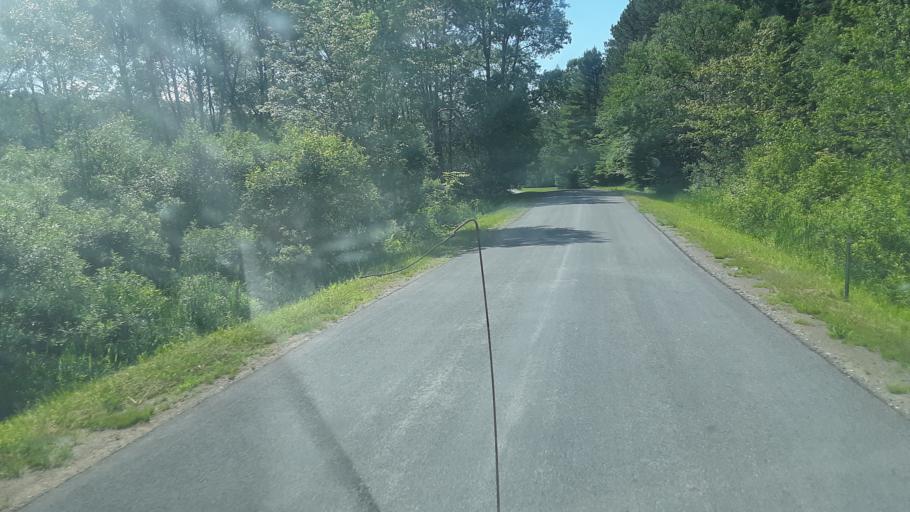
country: US
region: New York
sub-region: Oneida County
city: Rome
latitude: 43.3989
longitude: -75.5318
